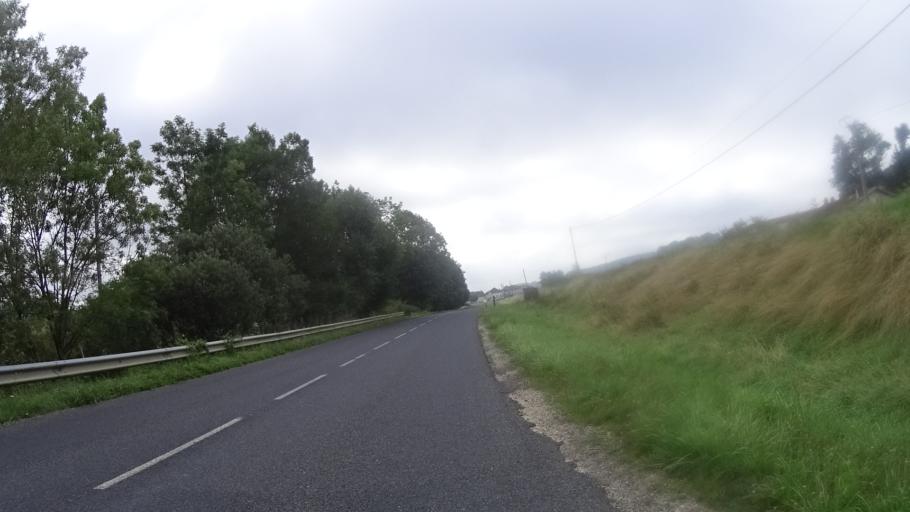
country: FR
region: Lorraine
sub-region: Departement de la Meuse
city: Fains-Veel
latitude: 48.7950
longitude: 5.1196
